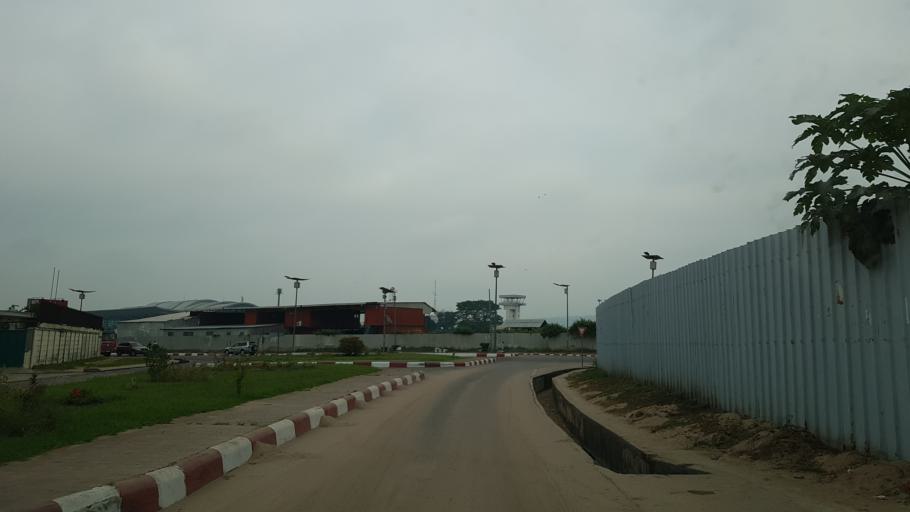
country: CG
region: Brazzaville
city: Brazzaville
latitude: -4.2583
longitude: 15.2562
